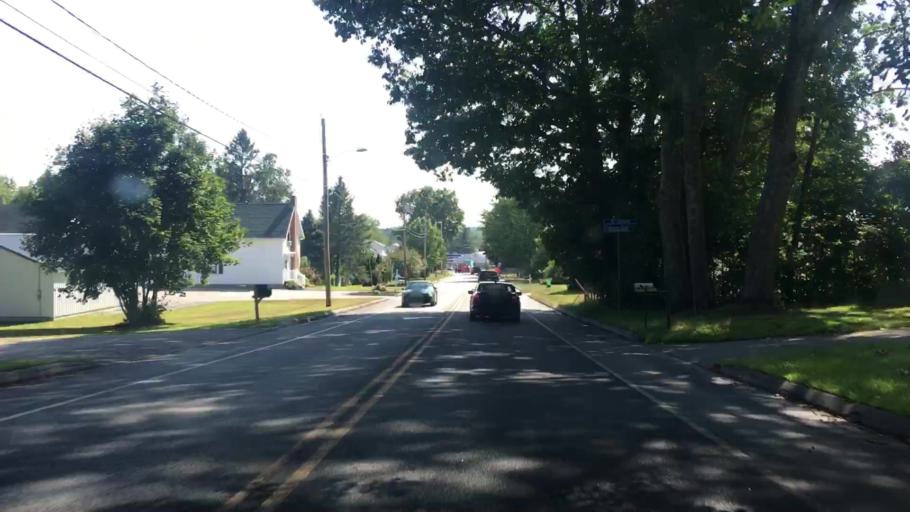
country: US
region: Maine
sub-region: Androscoggin County
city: Lisbon Falls
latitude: 44.0071
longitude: -70.0700
